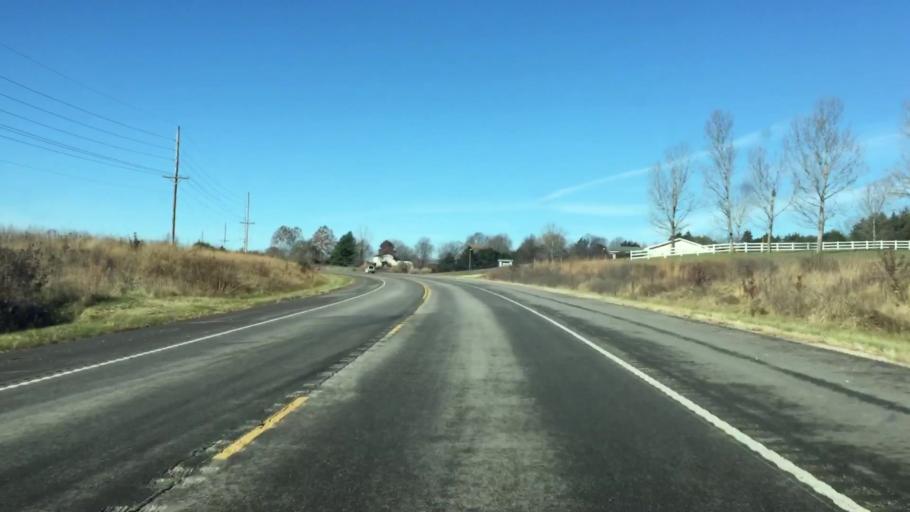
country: US
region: Missouri
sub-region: Miller County
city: Eldon
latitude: 38.3731
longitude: -92.6213
